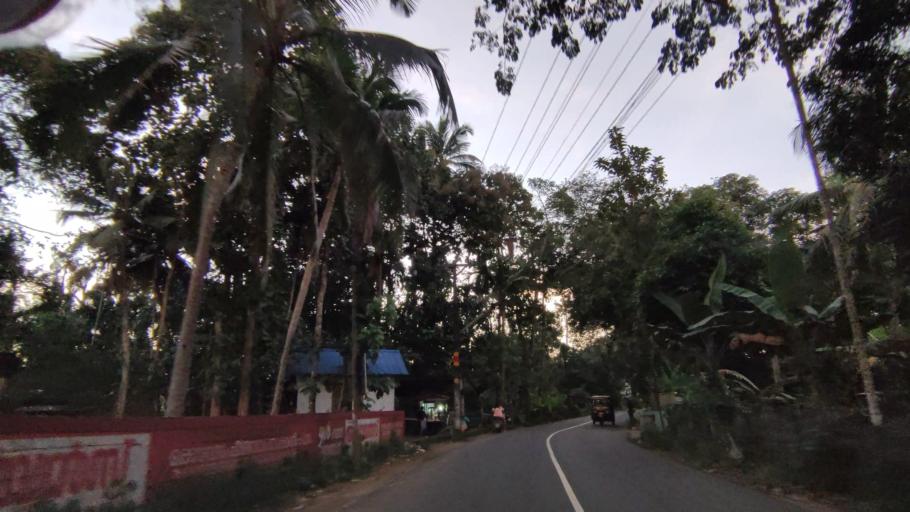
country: IN
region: Kerala
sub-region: Kottayam
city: Kottayam
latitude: 9.6893
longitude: 76.4989
